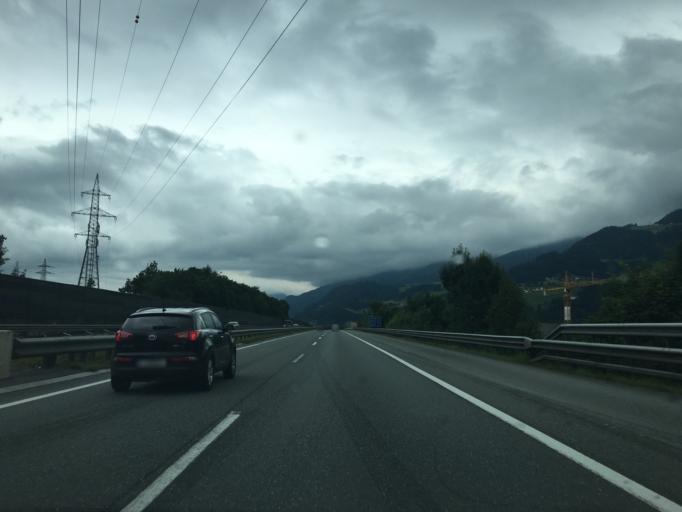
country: AT
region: Tyrol
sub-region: Politischer Bezirk Schwaz
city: Stans
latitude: 47.3626
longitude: 11.7135
